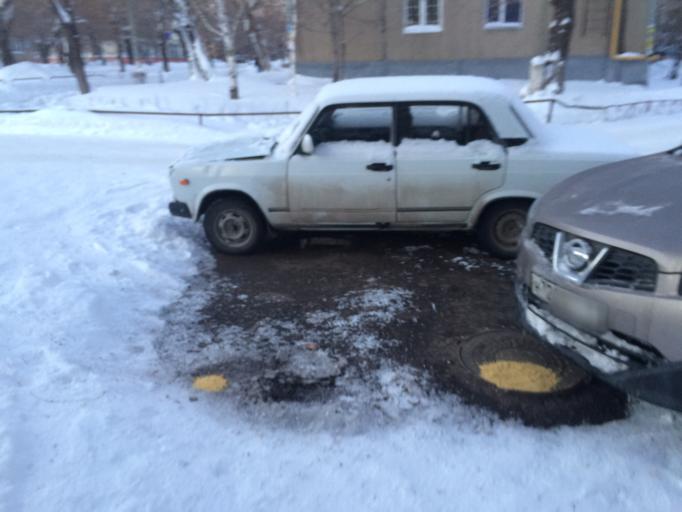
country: RU
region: Chelyabinsk
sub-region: Gorod Magnitogorsk
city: Magnitogorsk
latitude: 53.4060
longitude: 58.9719
